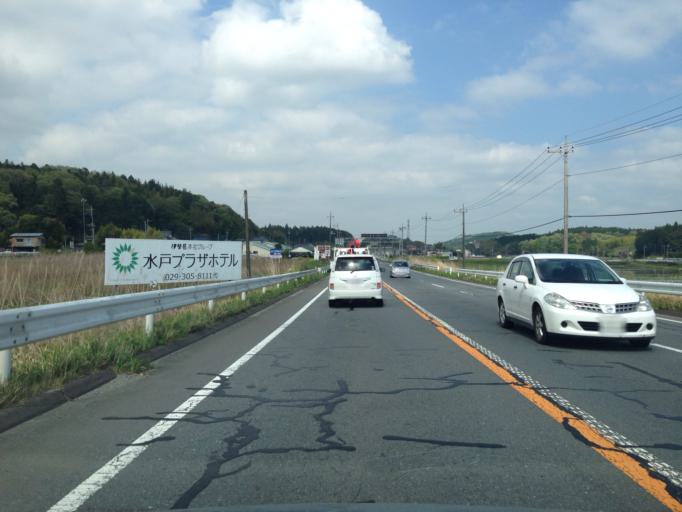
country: JP
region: Ibaraki
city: Kasama
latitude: 36.3552
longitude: 140.1919
